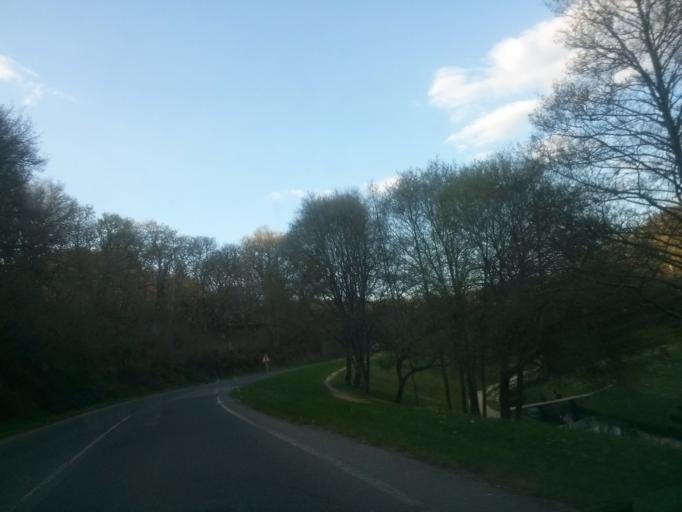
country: ES
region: Galicia
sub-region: Provincia de Lugo
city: Lugo
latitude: 42.9947
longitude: -7.5344
